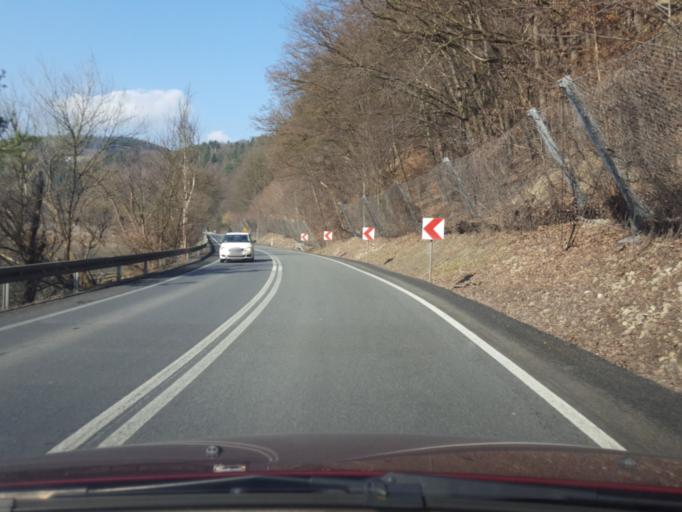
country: PL
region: Lesser Poland Voivodeship
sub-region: Powiat brzeski
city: Czchow
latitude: 49.8097
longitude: 20.6656
